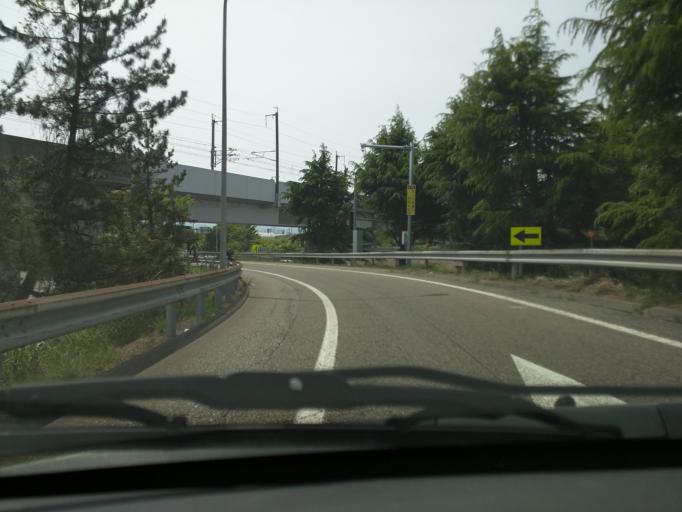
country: JP
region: Niigata
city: Tsubame
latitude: 37.6530
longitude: 138.9407
